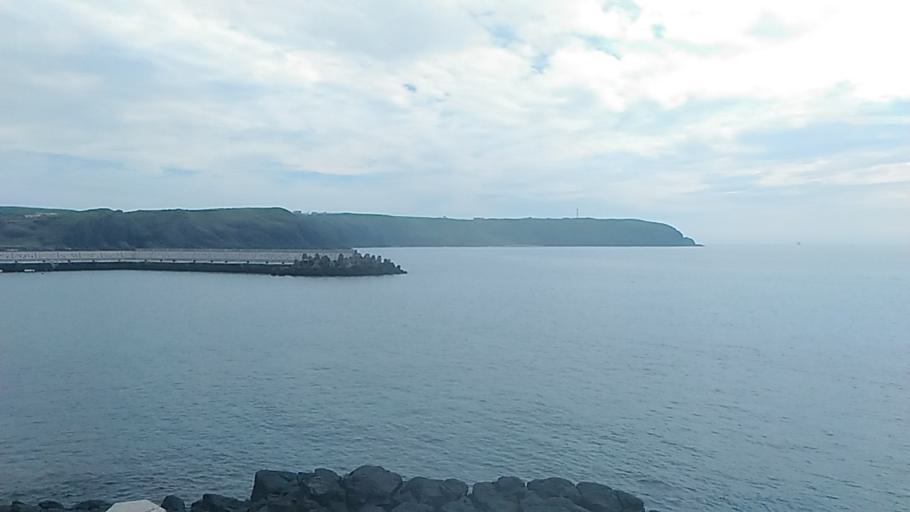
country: TW
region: Taiwan
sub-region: Penghu
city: Ma-kung
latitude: 23.1924
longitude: 119.4296
